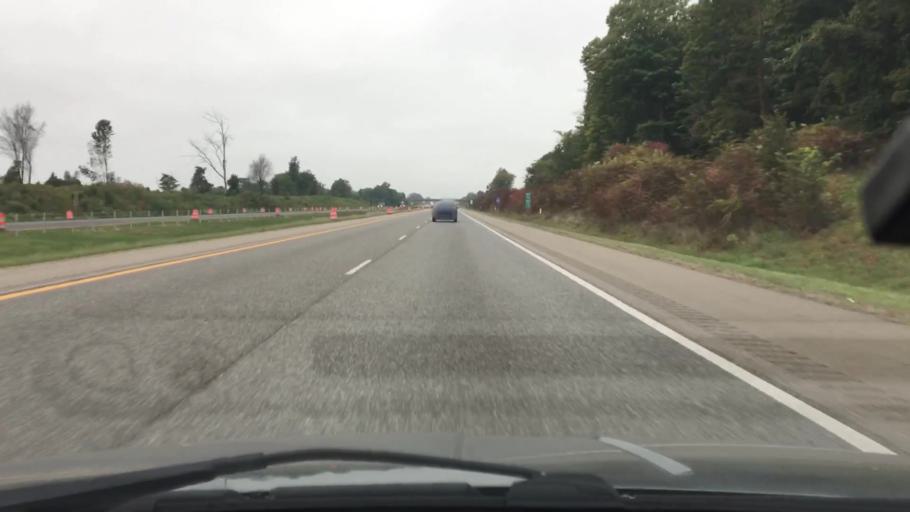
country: US
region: Michigan
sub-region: Van Buren County
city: Hartford
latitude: 42.1969
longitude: -86.0607
